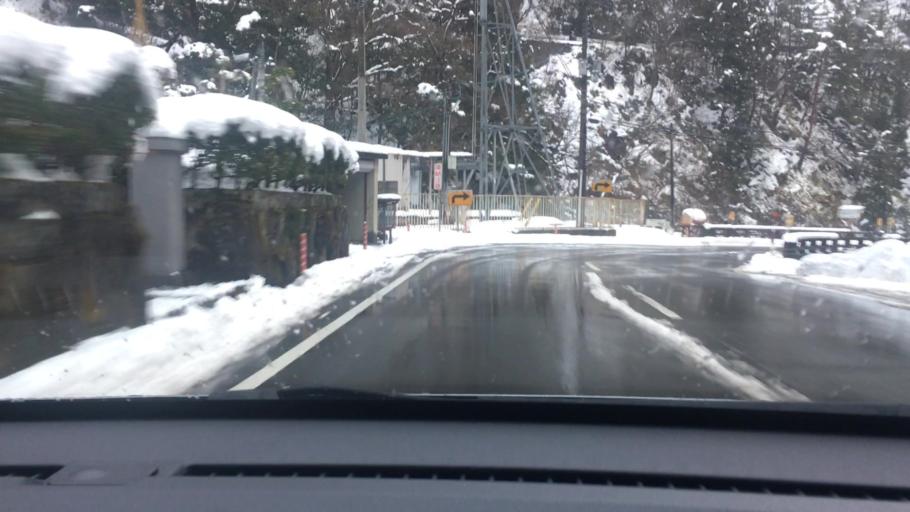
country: JP
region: Hyogo
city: Toyooka
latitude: 35.3692
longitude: 134.5830
